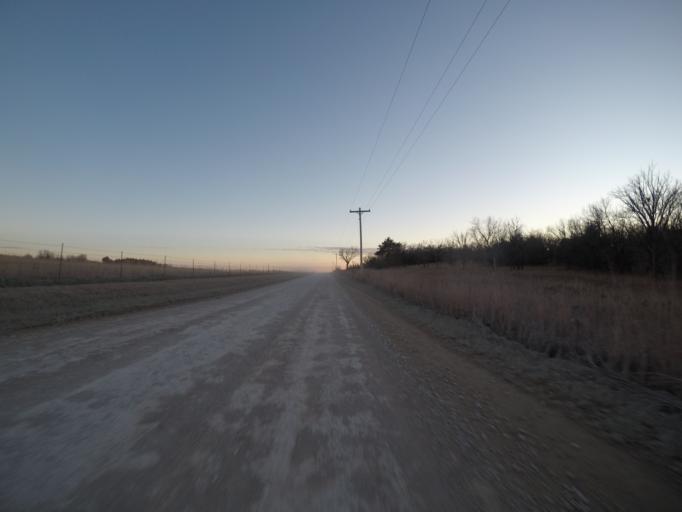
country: US
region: Kansas
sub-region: Riley County
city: Manhattan
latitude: 39.2397
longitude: -96.4826
